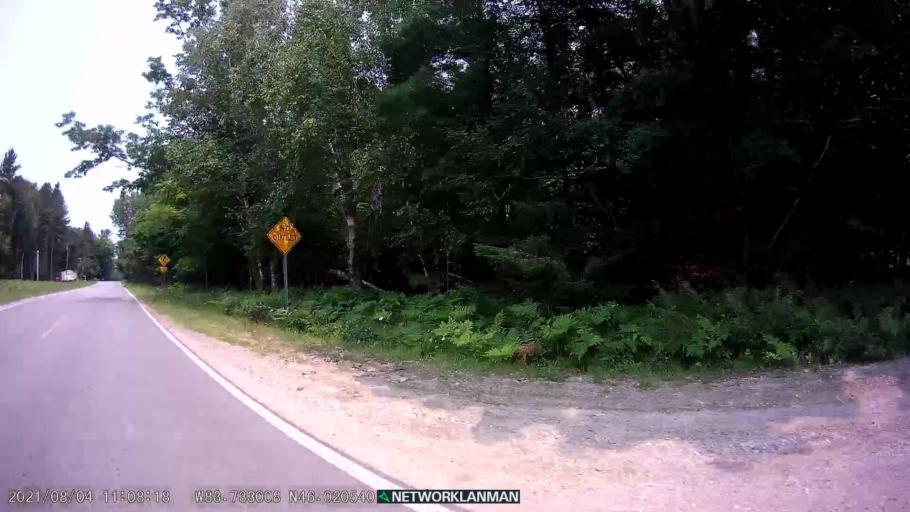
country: CA
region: Ontario
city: Thessalon
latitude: 46.0208
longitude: -83.7330
